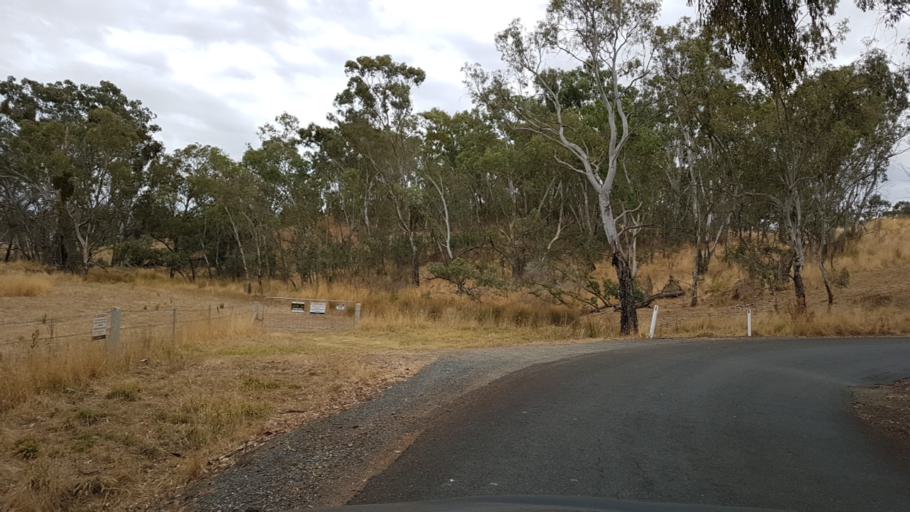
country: AU
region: South Australia
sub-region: Adelaide Hills
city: Gumeracha
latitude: -34.8140
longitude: 138.8092
